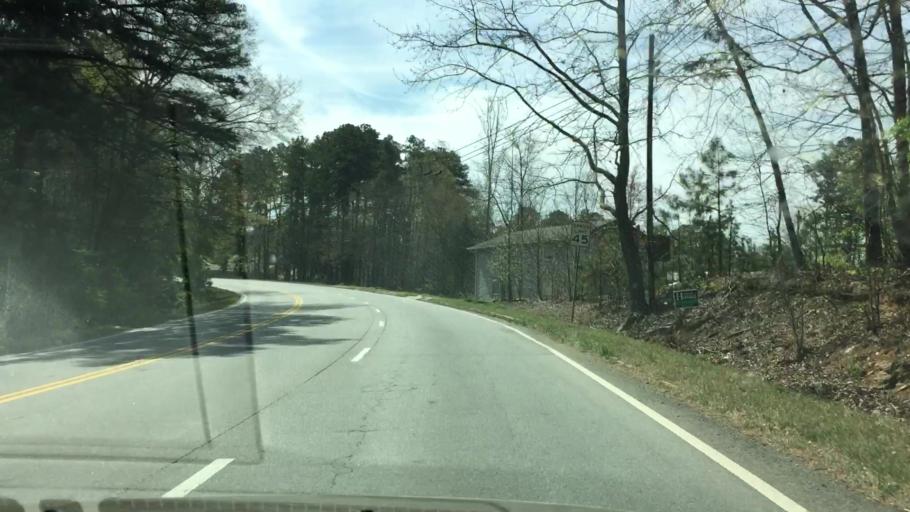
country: US
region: Georgia
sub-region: Barrow County
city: Winder
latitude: 34.0210
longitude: -83.7106
